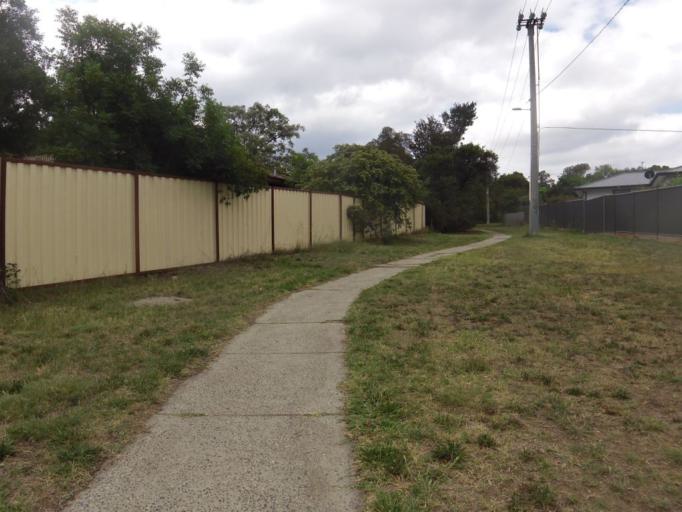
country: AU
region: Australian Capital Territory
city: Macarthur
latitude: -35.4031
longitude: 149.1289
